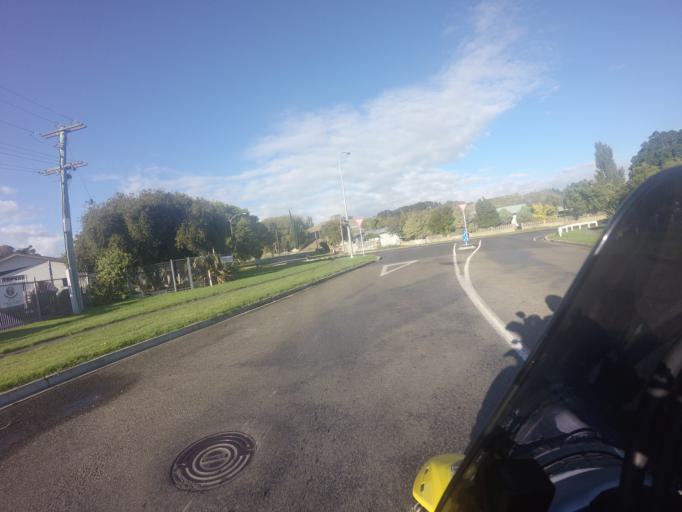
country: NZ
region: Gisborne
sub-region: Gisborne District
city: Gisborne
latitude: -38.6760
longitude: 178.0484
